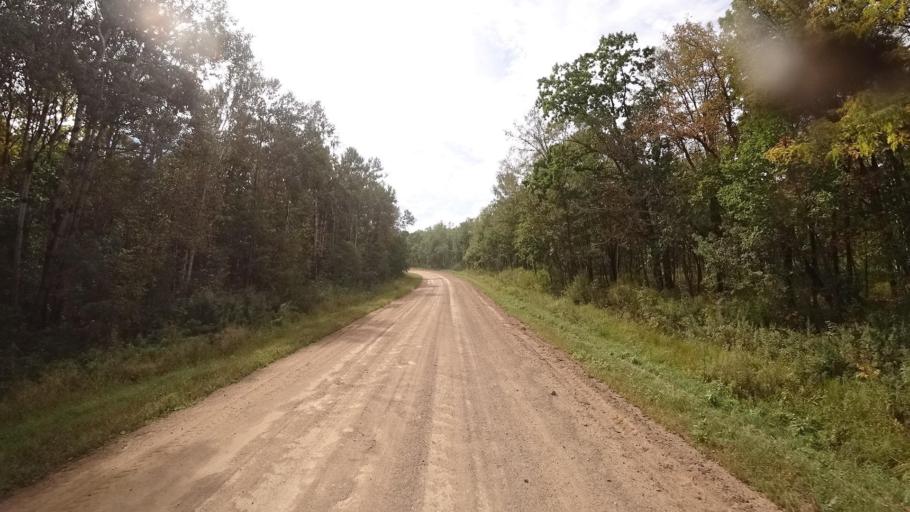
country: RU
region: Primorskiy
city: Yakovlevka
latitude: 44.5545
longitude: 133.5837
